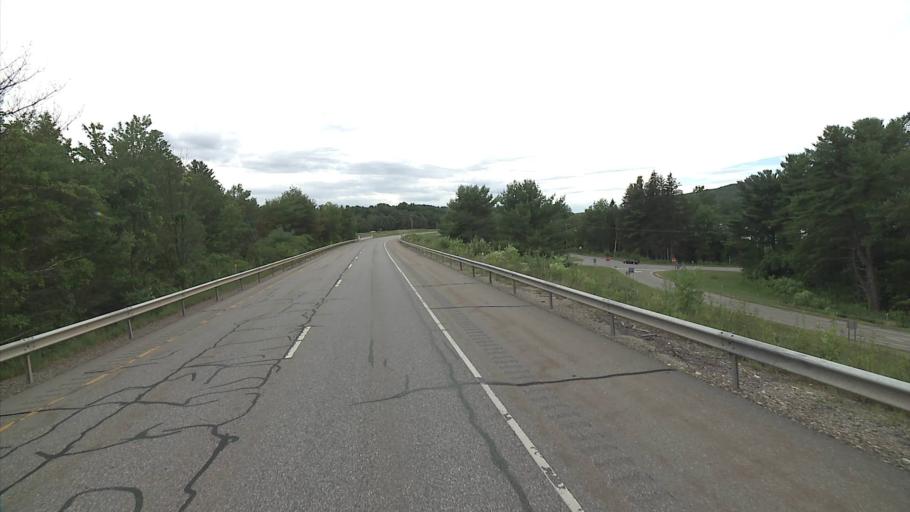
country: US
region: Connecticut
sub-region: Litchfield County
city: Winsted
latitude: 41.8797
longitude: -73.0718
